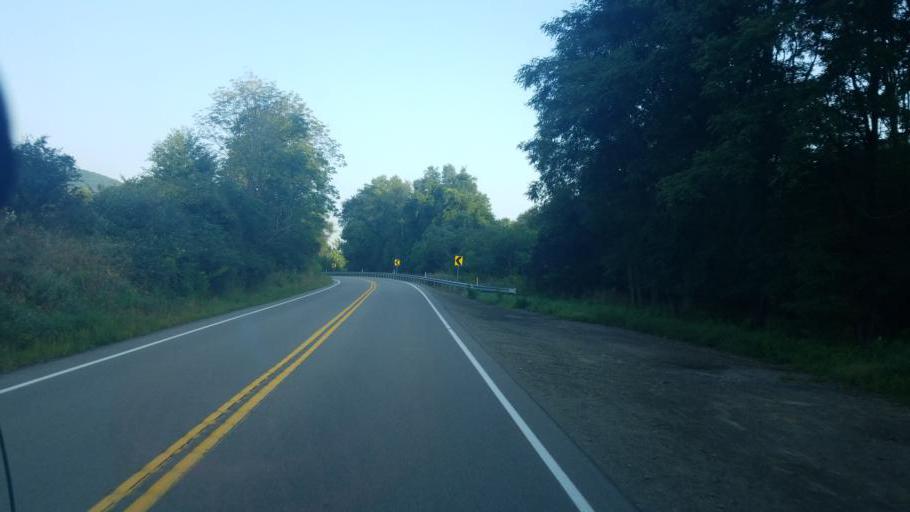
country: US
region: Pennsylvania
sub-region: Tioga County
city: Westfield
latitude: 41.9670
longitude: -77.4476
